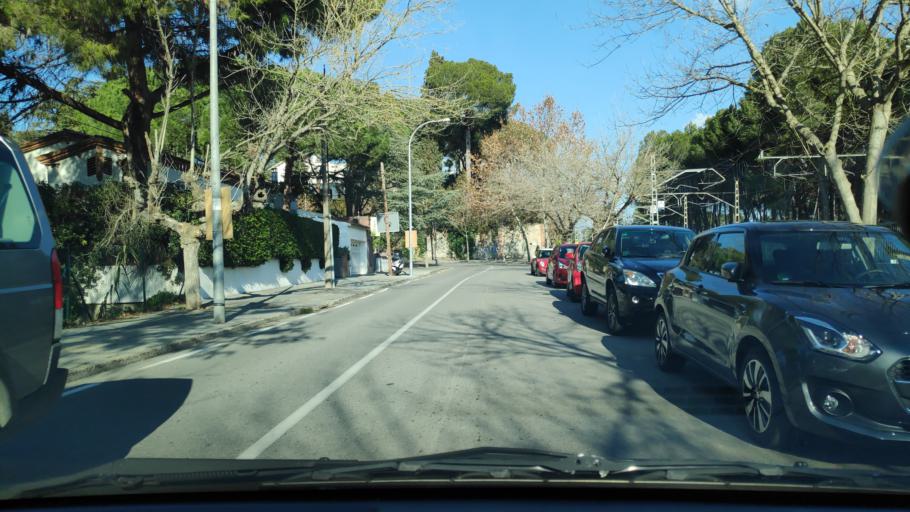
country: ES
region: Catalonia
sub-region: Provincia de Barcelona
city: Sant Quirze del Valles
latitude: 41.5013
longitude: 2.0909
